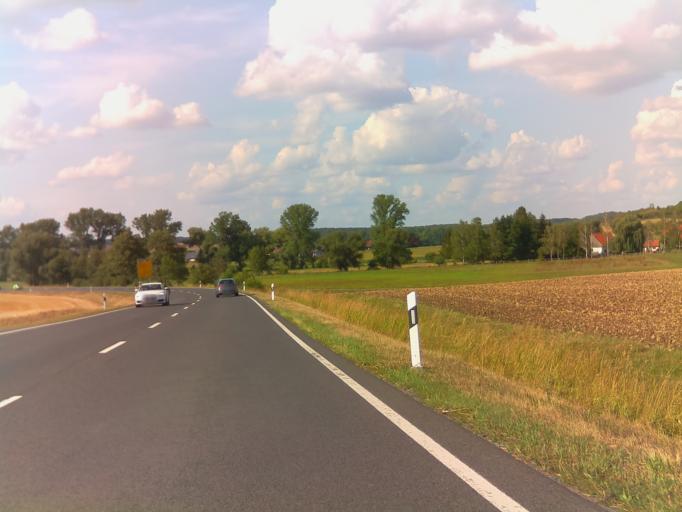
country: DE
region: Bavaria
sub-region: Regierungsbezirk Unterfranken
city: Bad Konigshofen im Grabfeld
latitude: 50.2900
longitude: 10.4870
